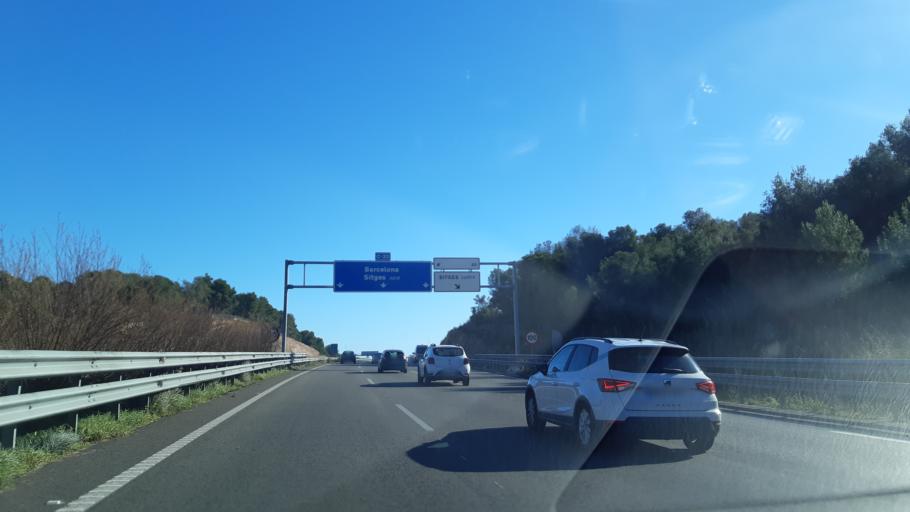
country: ES
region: Catalonia
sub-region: Provincia de Barcelona
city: Sitges
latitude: 41.2515
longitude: 1.8002
